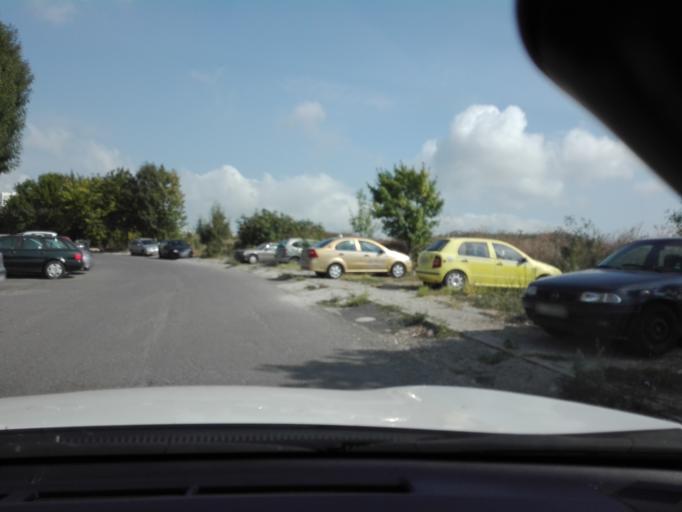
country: BG
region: Burgas
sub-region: Obshtina Burgas
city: Burgas
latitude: 42.4520
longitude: 27.4251
